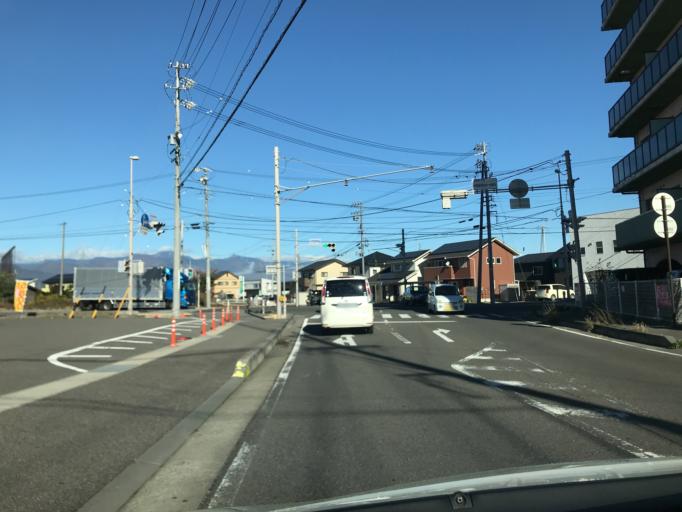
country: JP
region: Nagano
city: Shiojiri
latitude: 36.1182
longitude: 137.9462
